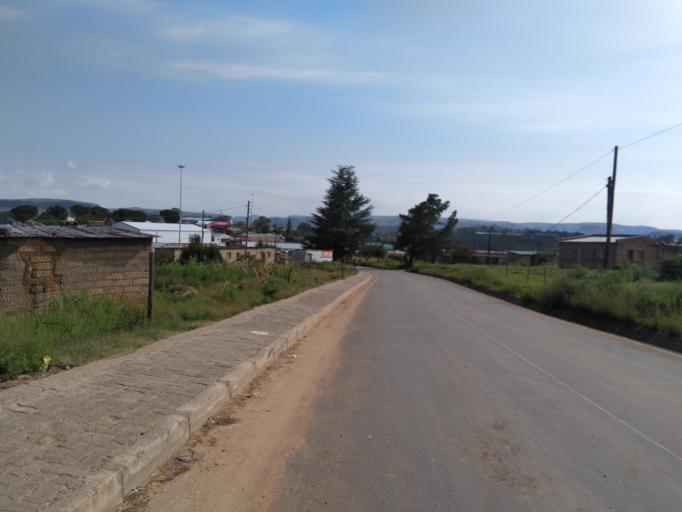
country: LS
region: Butha-Buthe
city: Butha-Buthe
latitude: -28.7713
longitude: 28.2502
